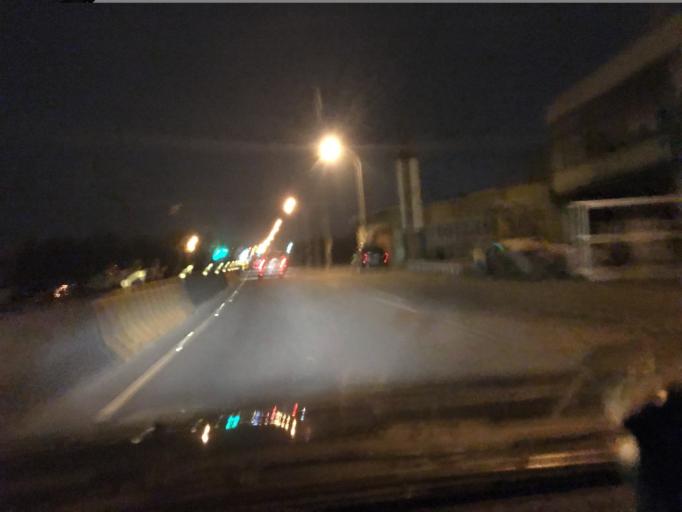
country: TW
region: Taiwan
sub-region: Hsinchu
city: Zhubei
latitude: 24.7944
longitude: 121.0569
